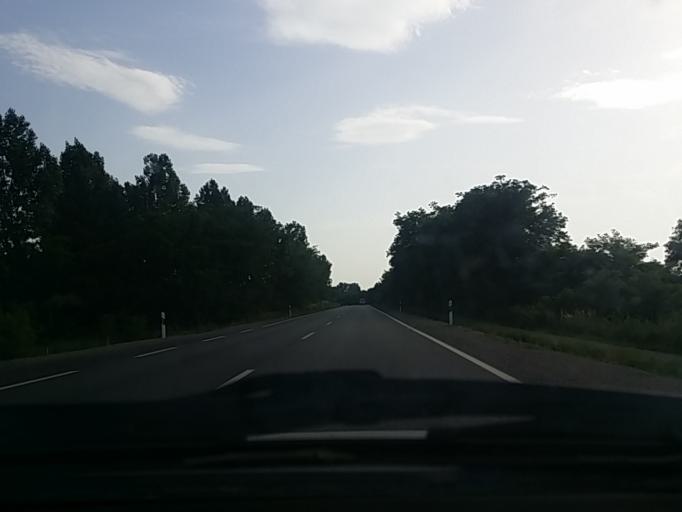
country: HU
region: Jasz-Nagykun-Szolnok
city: Jaszbereny
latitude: 47.4652
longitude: 19.8507
